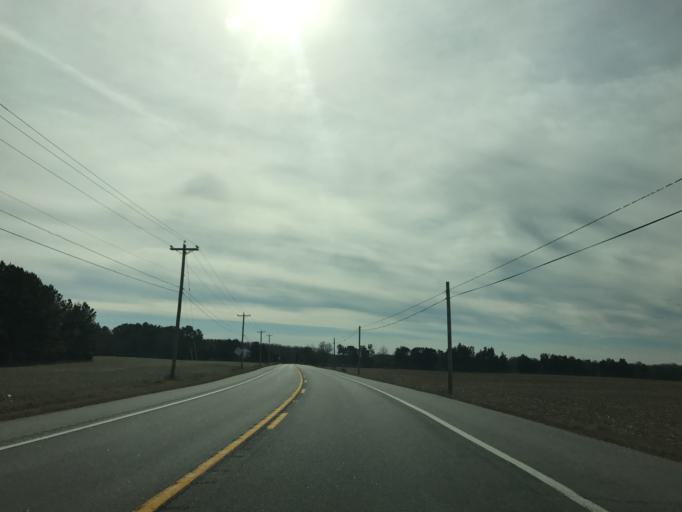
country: US
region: Maryland
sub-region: Queen Anne's County
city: Centreville
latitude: 39.1158
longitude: -76.0216
